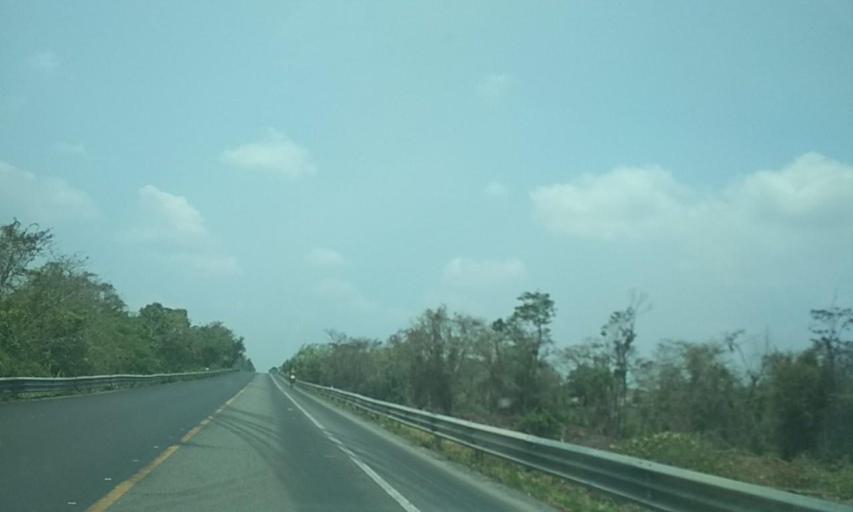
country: MX
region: Tabasco
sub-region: Huimanguillo
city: Francisco Rueda
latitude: 17.7119
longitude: -93.9421
